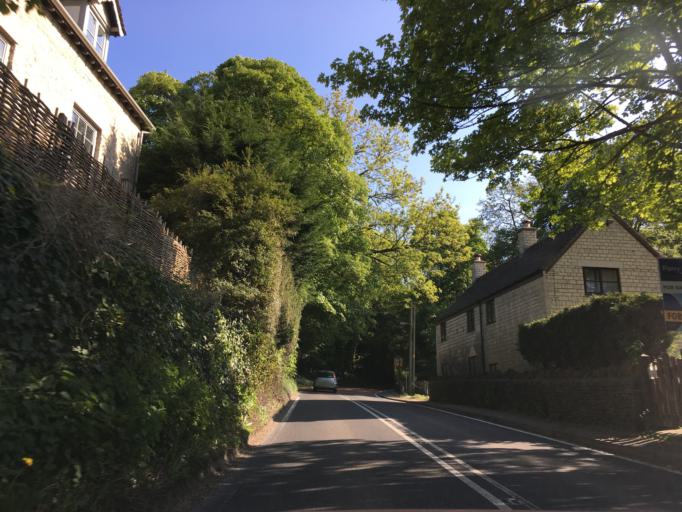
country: GB
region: England
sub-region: Gloucestershire
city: Nailsworth
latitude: 51.6901
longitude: -2.2215
